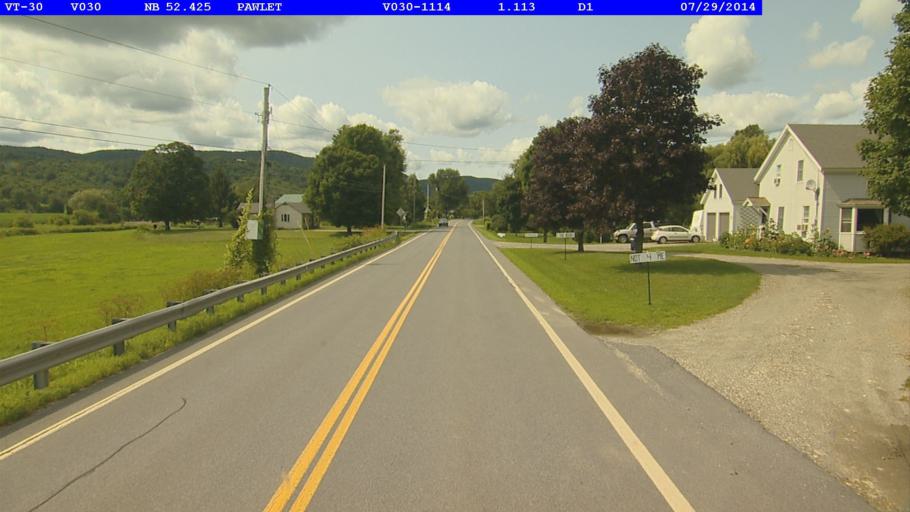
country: US
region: New York
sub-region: Washington County
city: Granville
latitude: 43.3268
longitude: -73.1719
